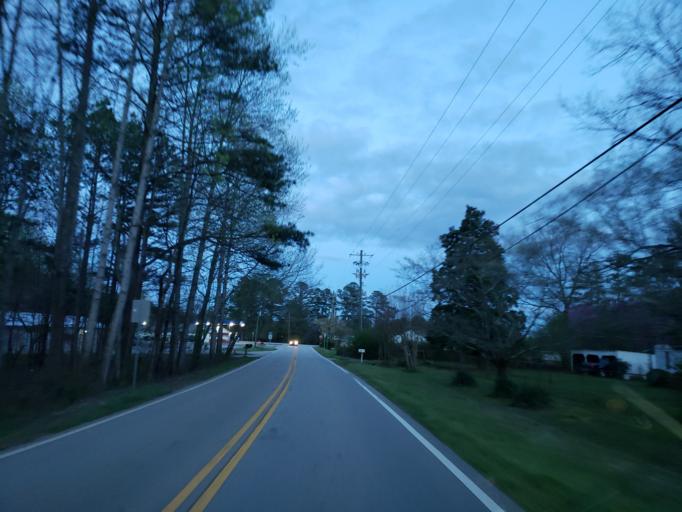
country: US
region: Georgia
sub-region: Paulding County
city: Dallas
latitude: 34.0150
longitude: -84.8633
